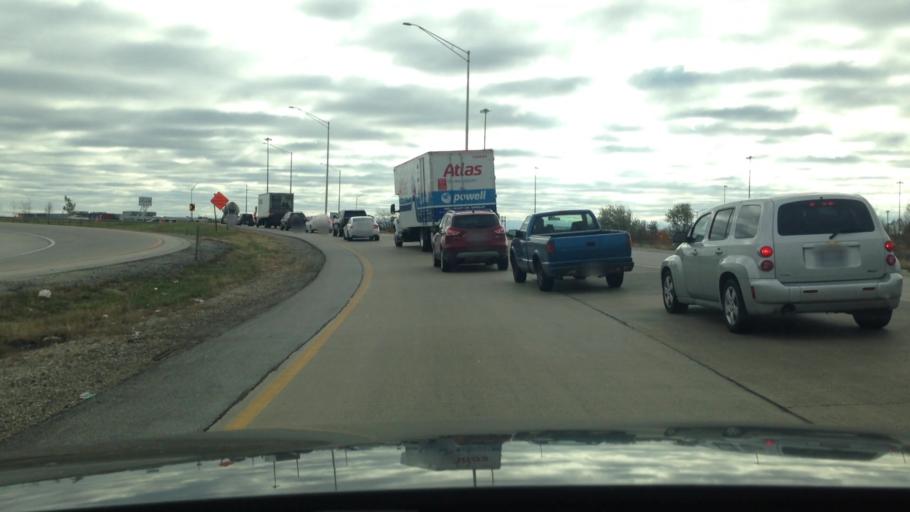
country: US
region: Illinois
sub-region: Cook County
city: Rolling Meadows
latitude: 42.0562
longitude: -88.0313
